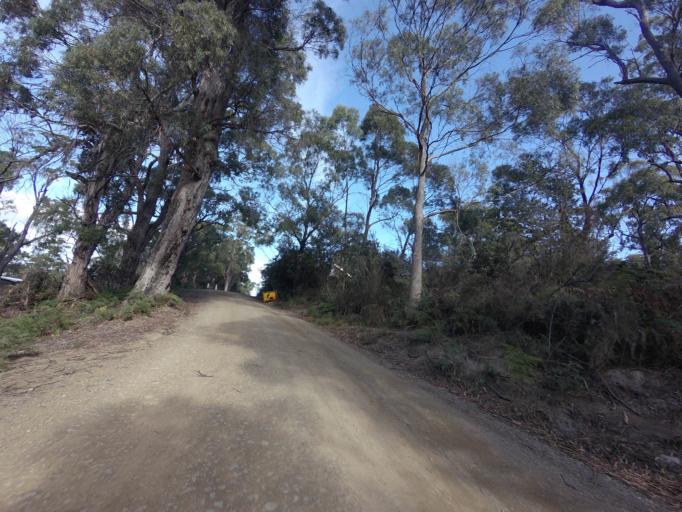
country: AU
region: Tasmania
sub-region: Clarence
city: Sandford
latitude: -42.9915
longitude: 147.7130
